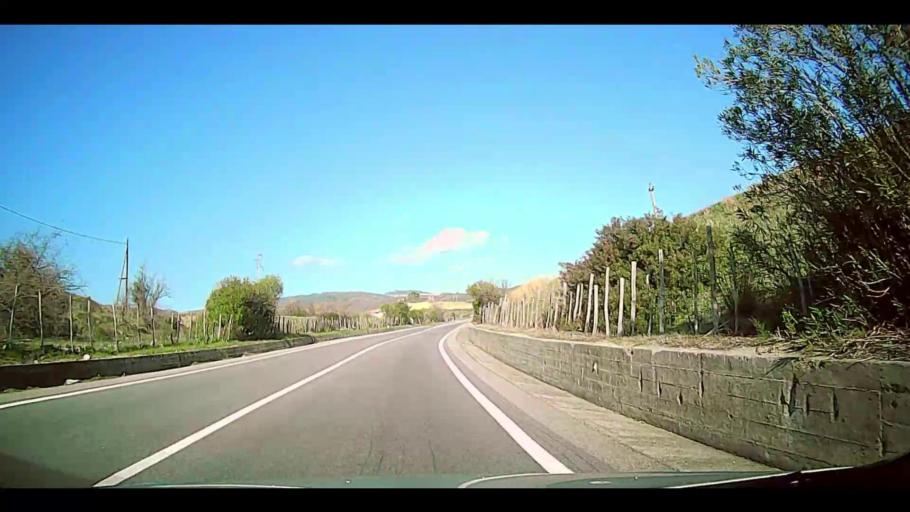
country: IT
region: Calabria
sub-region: Provincia di Crotone
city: Cotronei
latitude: 39.1874
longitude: 16.8176
